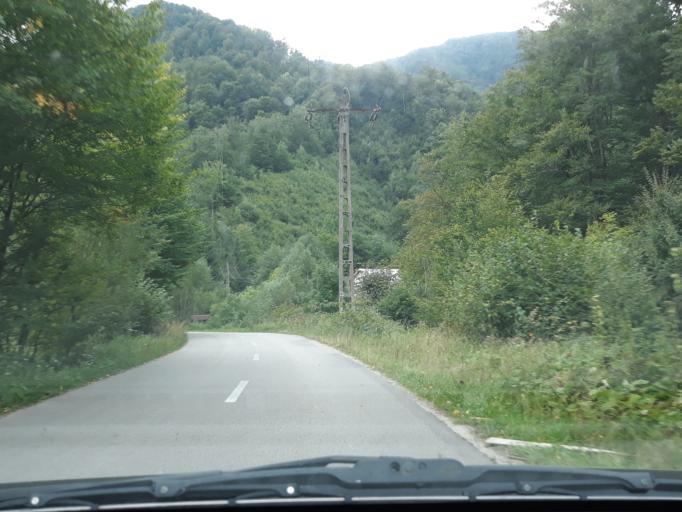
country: RO
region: Bihor
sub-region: Comuna Pietroasa
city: Pietroasa
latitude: 46.5906
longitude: 22.6319
